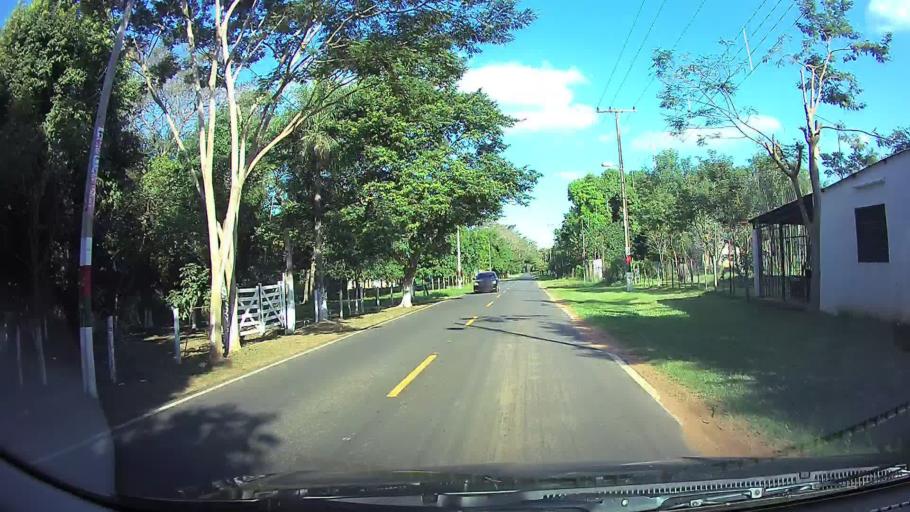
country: PY
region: Central
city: Aregua
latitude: -25.2881
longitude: -57.3951
